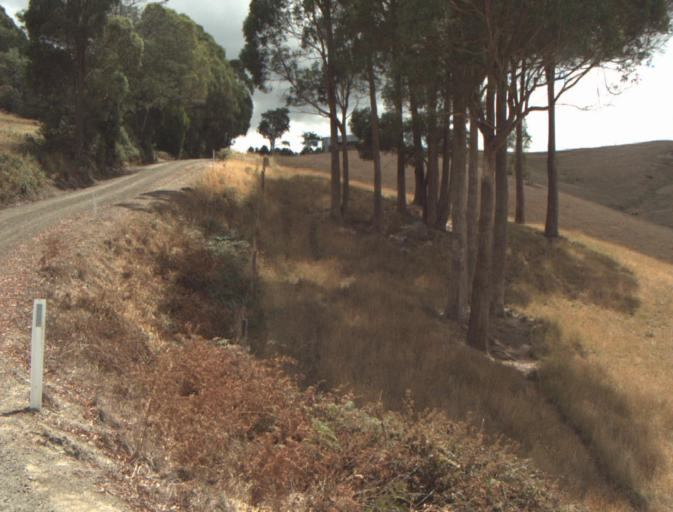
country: AU
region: Tasmania
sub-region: Launceston
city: Mayfield
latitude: -41.2090
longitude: 147.1401
